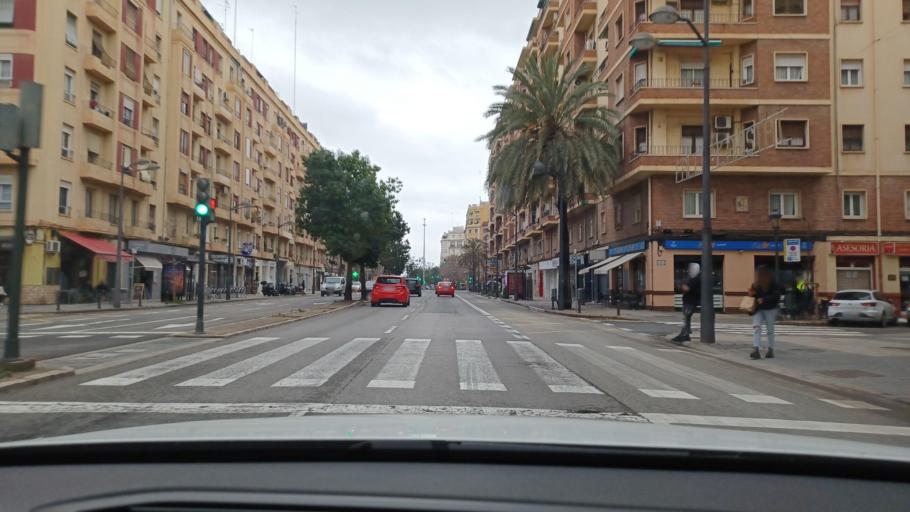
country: ES
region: Valencia
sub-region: Provincia de Valencia
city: Valencia
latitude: 39.4738
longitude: -0.3532
